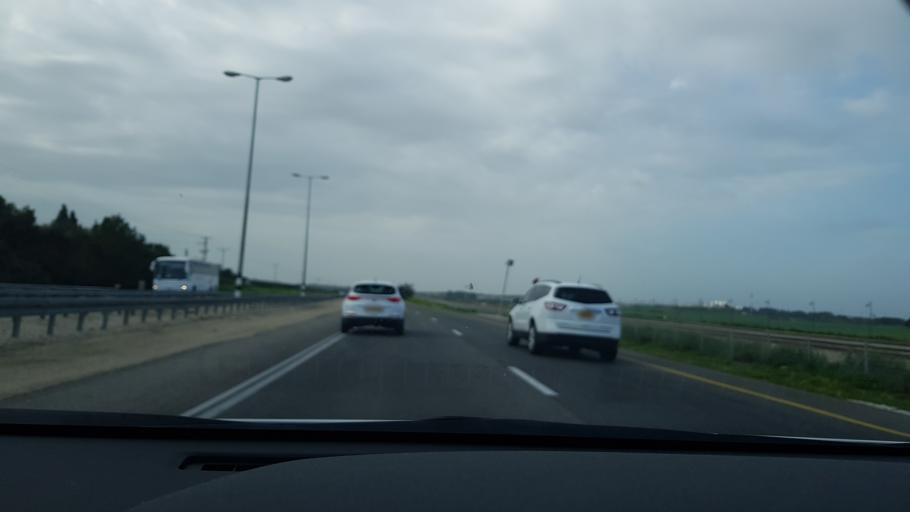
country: IL
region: Southern District
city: Ashdod
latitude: 31.7189
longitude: 34.6316
